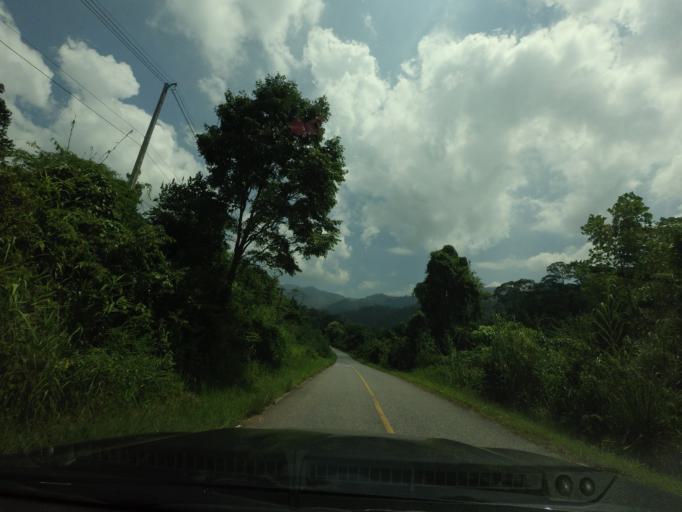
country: TH
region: Loei
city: Na Haeo
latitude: 17.6991
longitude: 100.9425
